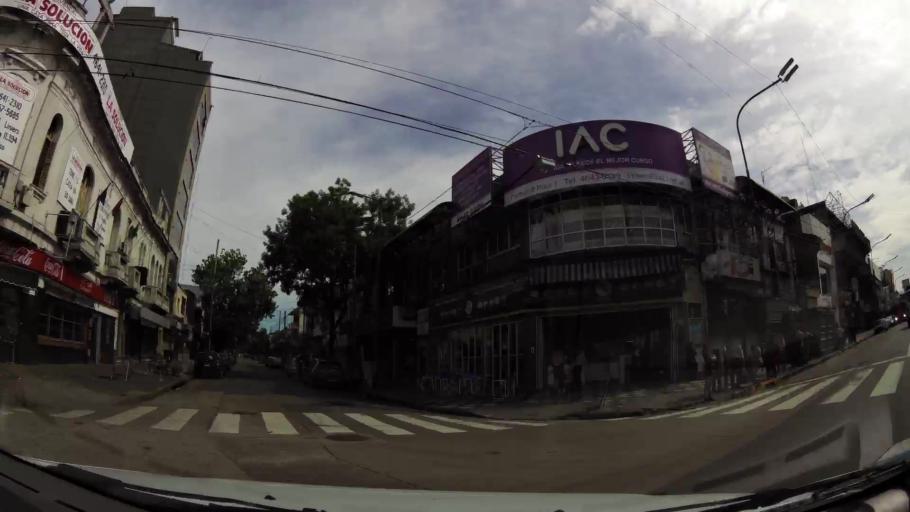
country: AR
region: Buenos Aires
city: San Justo
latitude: -34.6392
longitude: -58.5252
